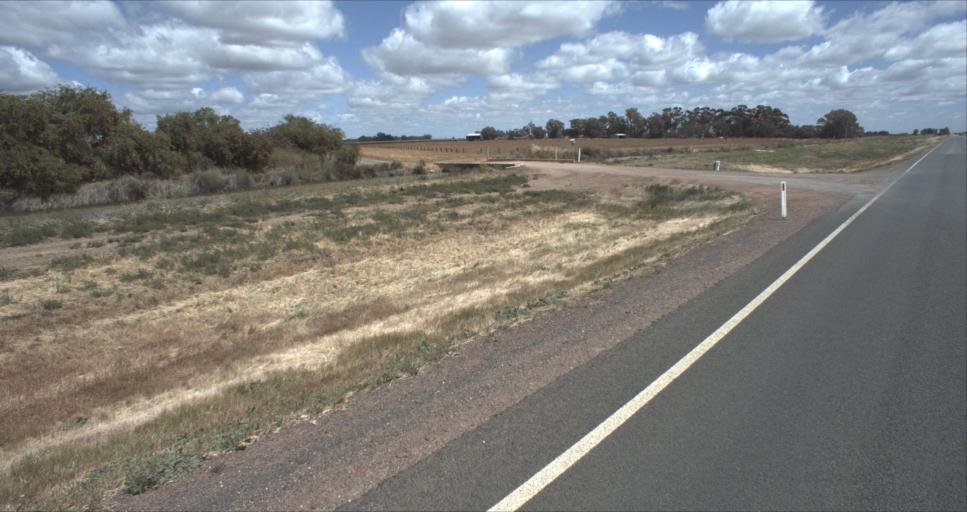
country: AU
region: New South Wales
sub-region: Murrumbidgee Shire
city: Darlington Point
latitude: -34.4864
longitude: 146.1600
